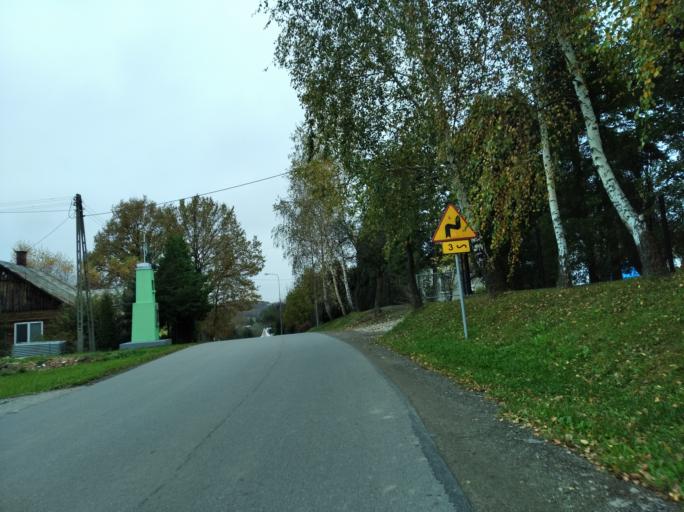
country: PL
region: Subcarpathian Voivodeship
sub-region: Powiat krosnienski
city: Jedlicze
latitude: 49.7298
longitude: 21.6520
